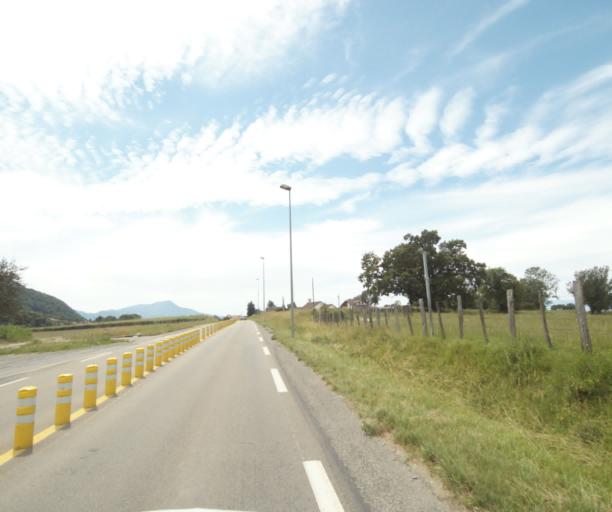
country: FR
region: Rhone-Alpes
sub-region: Departement de la Haute-Savoie
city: Allinges
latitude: 46.3346
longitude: 6.4523
